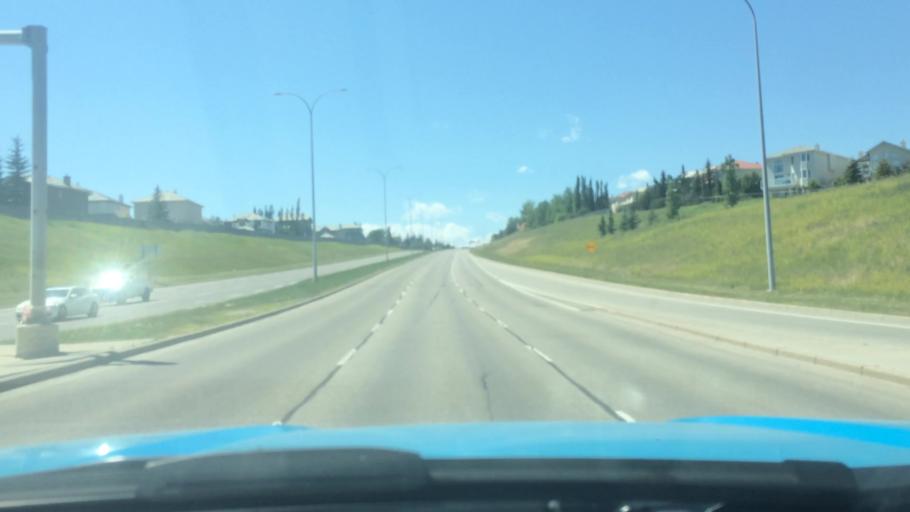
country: CA
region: Alberta
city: Calgary
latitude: 51.1424
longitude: -114.1250
